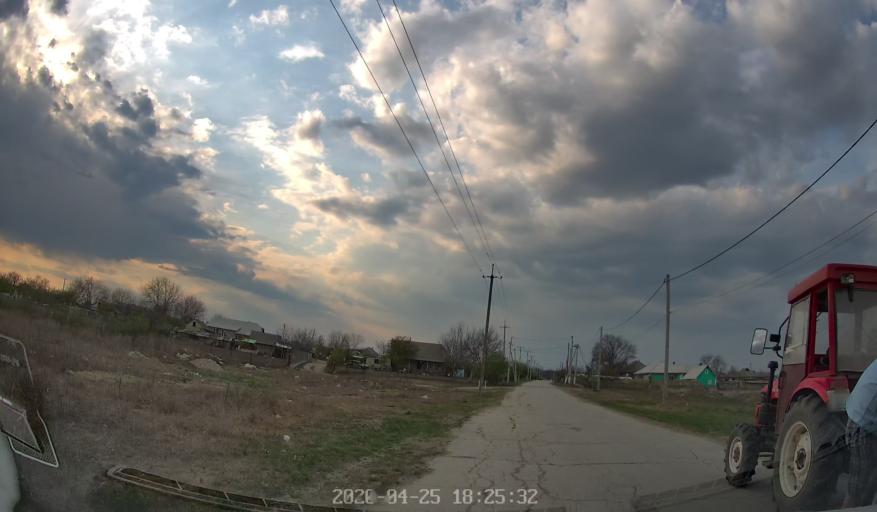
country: MD
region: Criuleni
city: Criuleni
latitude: 47.1620
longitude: 29.1288
